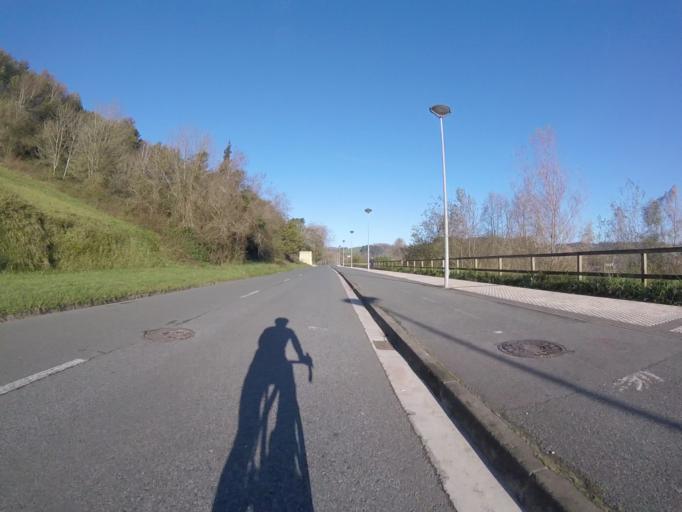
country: ES
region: Basque Country
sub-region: Provincia de Guipuzcoa
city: Lasarte
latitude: 43.2685
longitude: -2.0263
